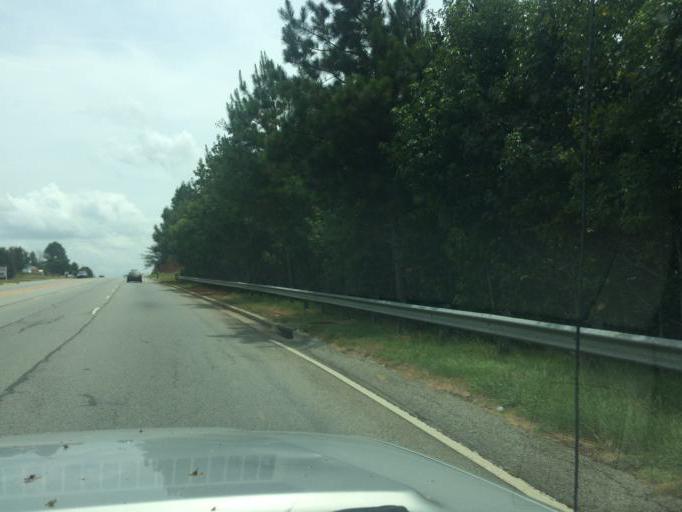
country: US
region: South Carolina
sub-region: Anderson County
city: Centerville
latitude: 34.5153
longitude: -82.7674
